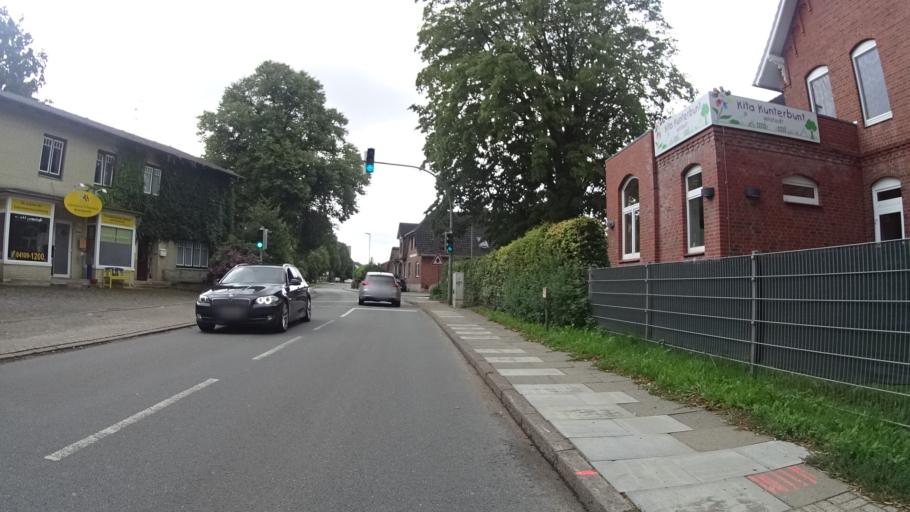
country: DE
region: Schleswig-Holstein
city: Tangstedt
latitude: 53.7484
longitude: 10.0668
